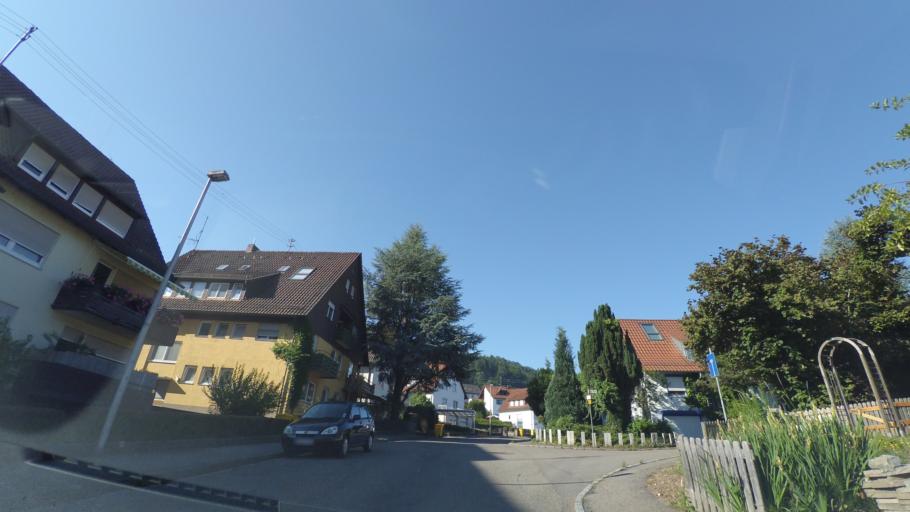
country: DE
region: Baden-Wuerttemberg
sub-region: Regierungsbezirk Stuttgart
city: Murrhardt
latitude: 48.9809
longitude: 9.5696
